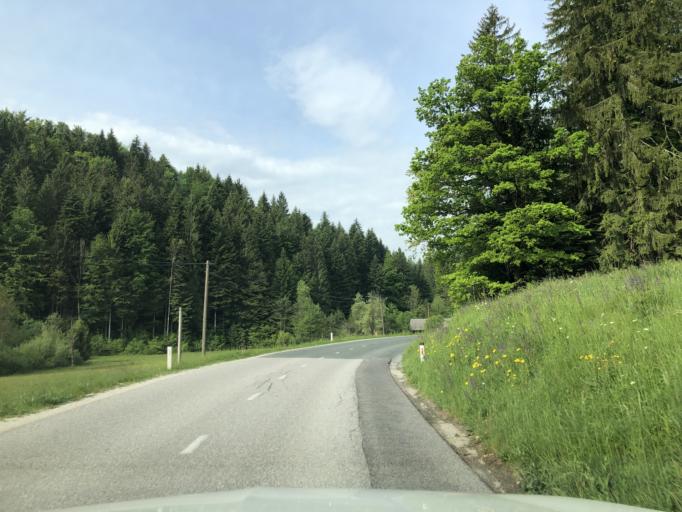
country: SI
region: Velike Lasce
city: Velike Lasce
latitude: 45.8241
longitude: 14.6307
